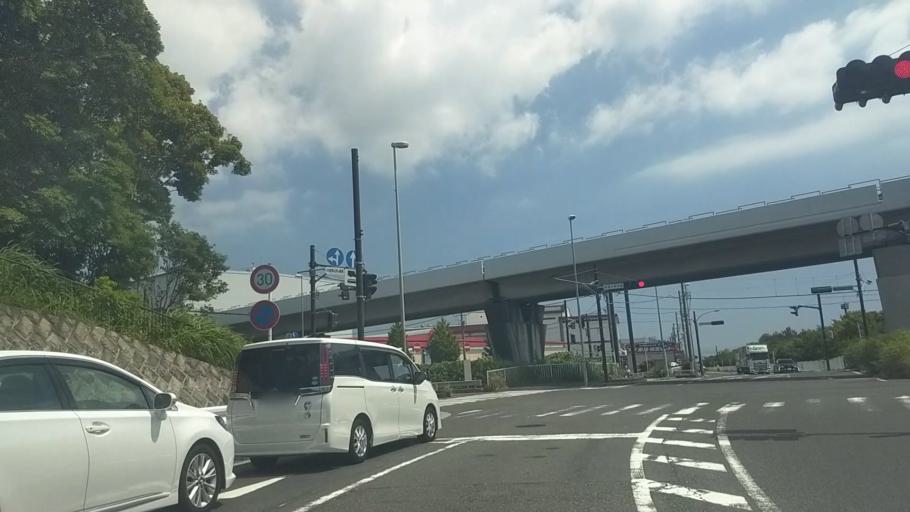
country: JP
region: Kanagawa
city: Yokosuka
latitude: 35.3547
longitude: 139.6433
